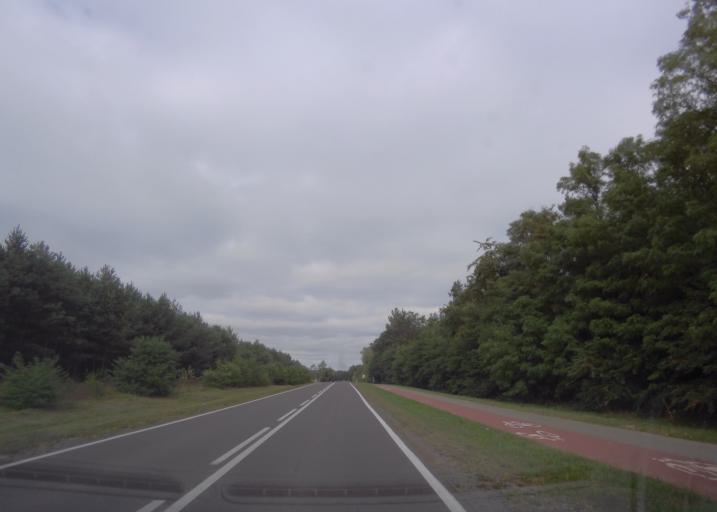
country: PL
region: Lublin Voivodeship
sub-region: Powiat wlodawski
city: Wlodawa
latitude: 51.5103
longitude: 23.5228
